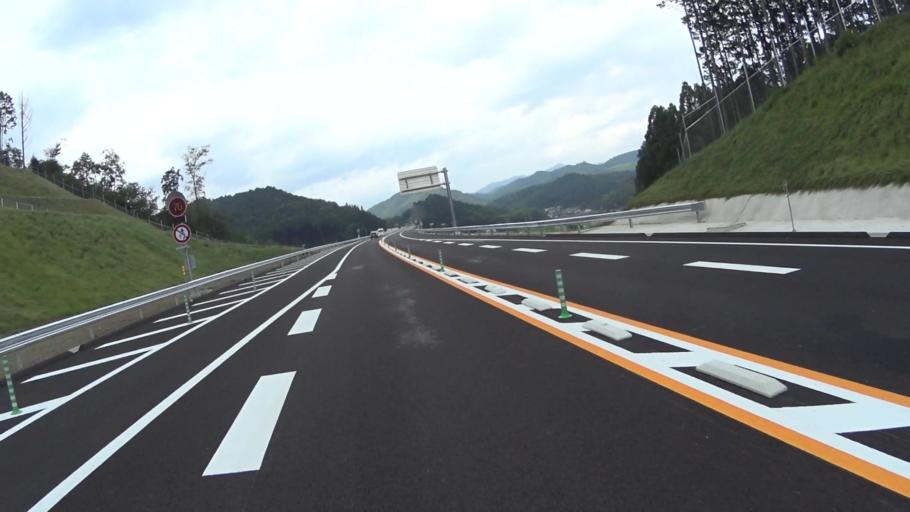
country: JP
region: Kyoto
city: Ayabe
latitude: 35.1879
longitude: 135.3599
